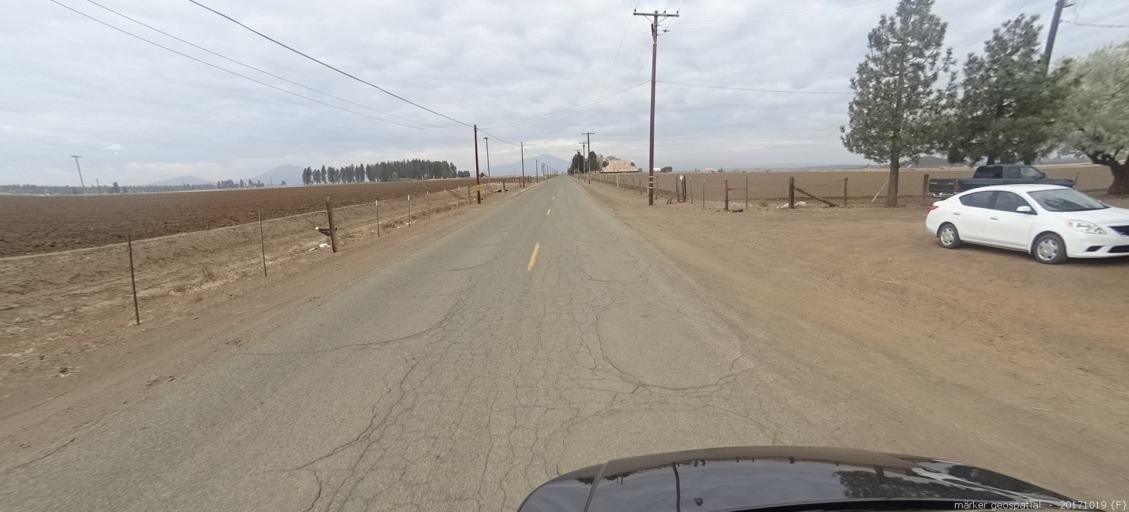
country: US
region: California
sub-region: Shasta County
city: Burney
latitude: 41.0806
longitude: -121.3408
